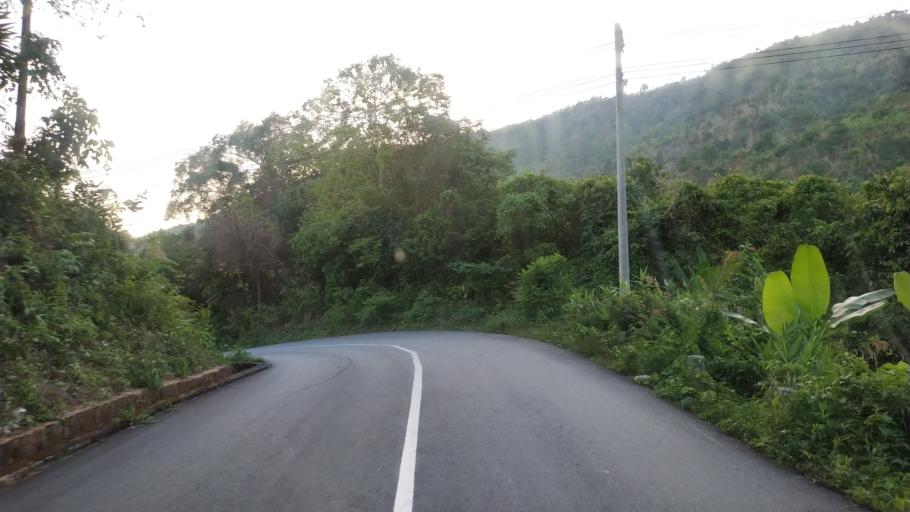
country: MM
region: Mon
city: Kyaikto
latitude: 17.4276
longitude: 97.0883
